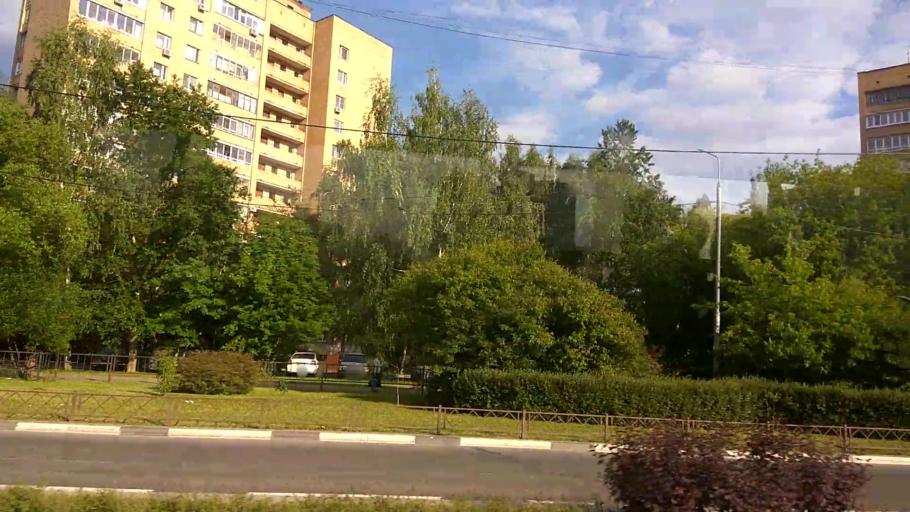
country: RU
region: Moskovskaya
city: Mytishchi
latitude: 55.9132
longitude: 37.7179
